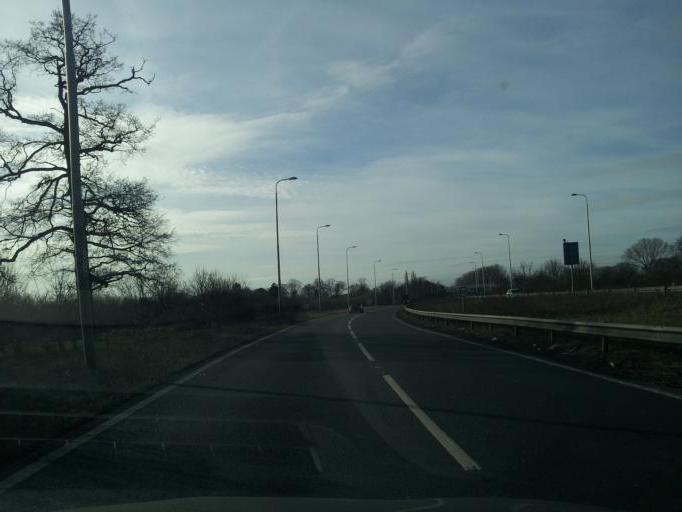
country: GB
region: England
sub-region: Central Bedfordshire
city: Tempsford
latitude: 52.1746
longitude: -0.2995
